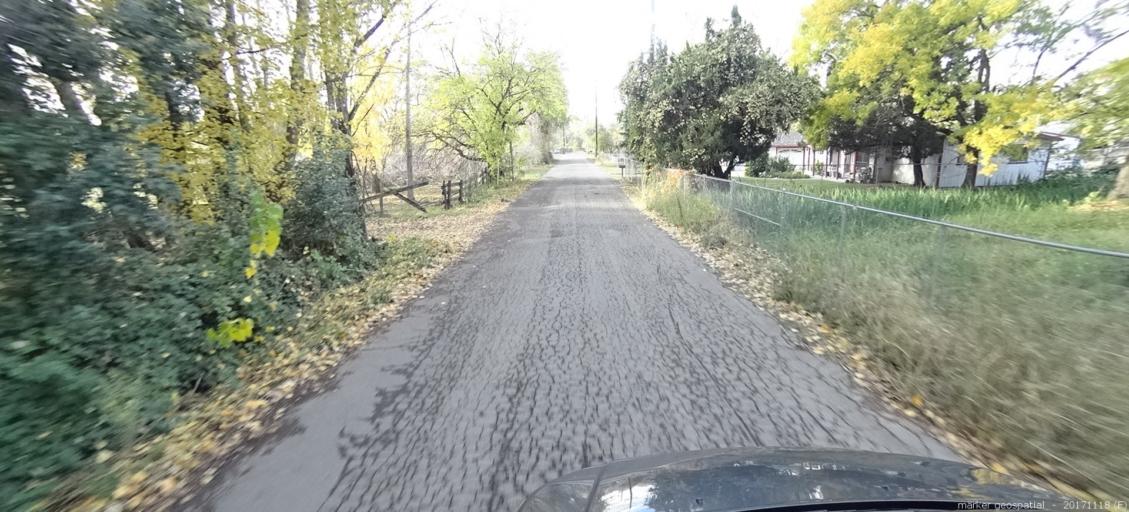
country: US
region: California
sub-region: Shasta County
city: Anderson
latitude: 40.4617
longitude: -122.3286
